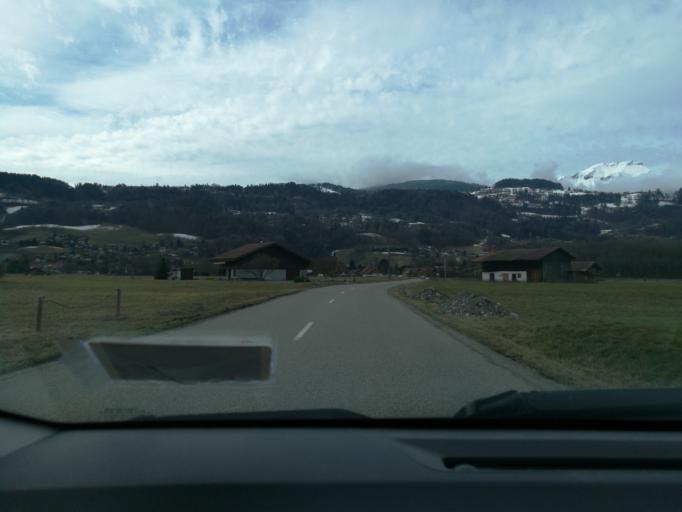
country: FR
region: Rhone-Alpes
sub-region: Departement de la Haute-Savoie
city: Domancy
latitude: 45.9164
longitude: 6.6641
